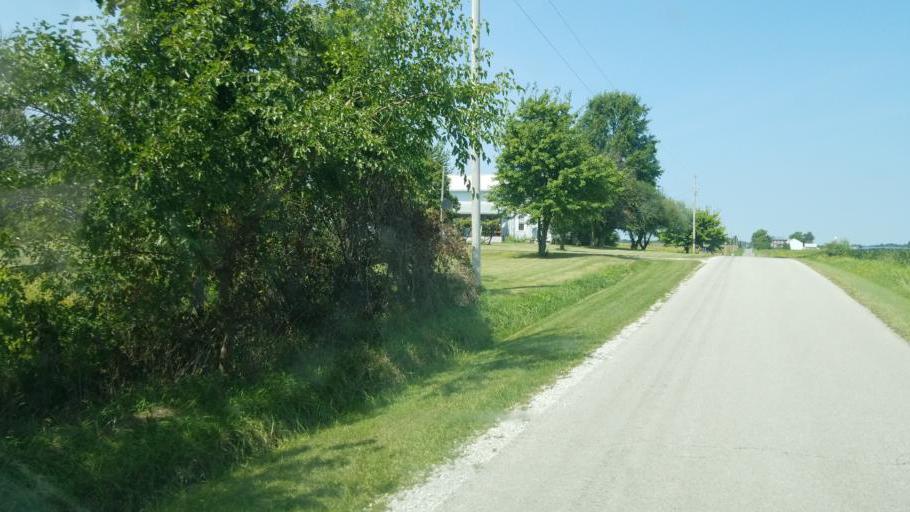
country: US
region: Ohio
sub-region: Crawford County
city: Bucyrus
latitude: 40.9040
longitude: -83.0741
